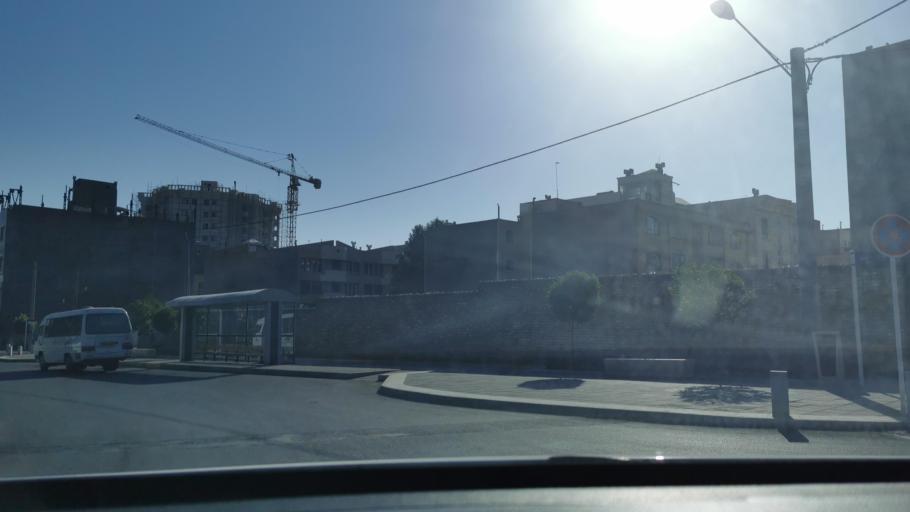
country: IR
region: Razavi Khorasan
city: Mashhad
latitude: 36.3100
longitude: 59.5130
